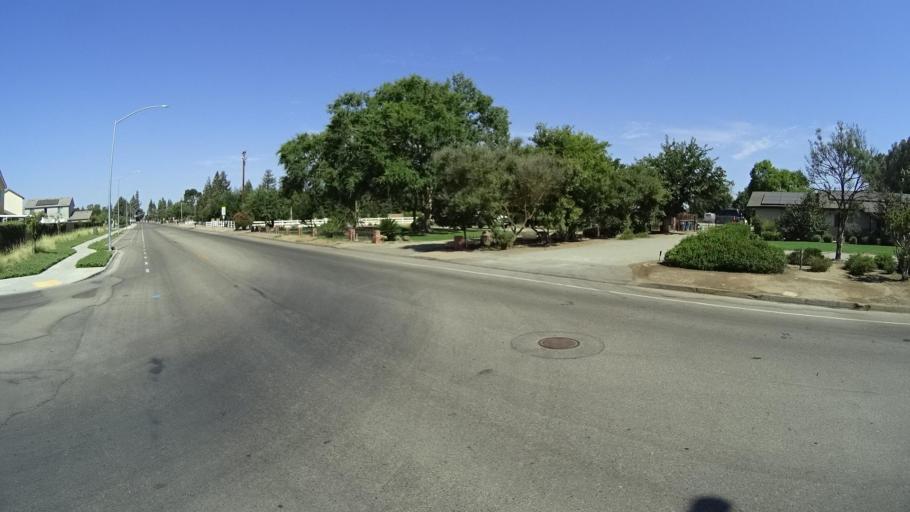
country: US
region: California
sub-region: Fresno County
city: Sunnyside
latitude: 36.7723
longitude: -119.6601
